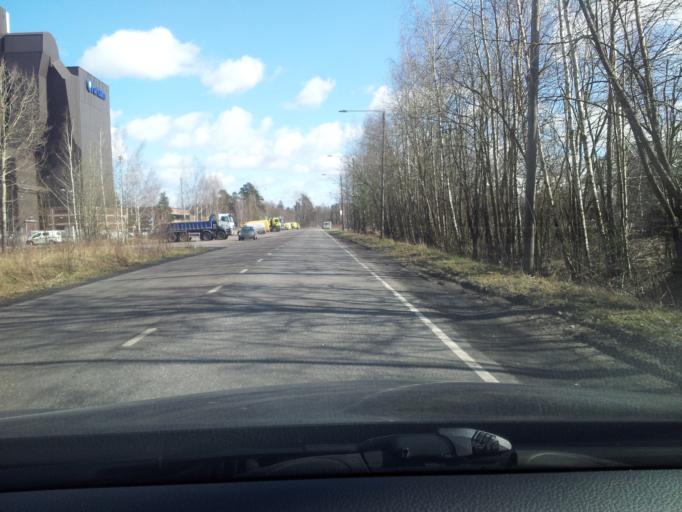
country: FI
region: Uusimaa
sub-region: Helsinki
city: Koukkuniemi
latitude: 60.1478
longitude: 24.7159
